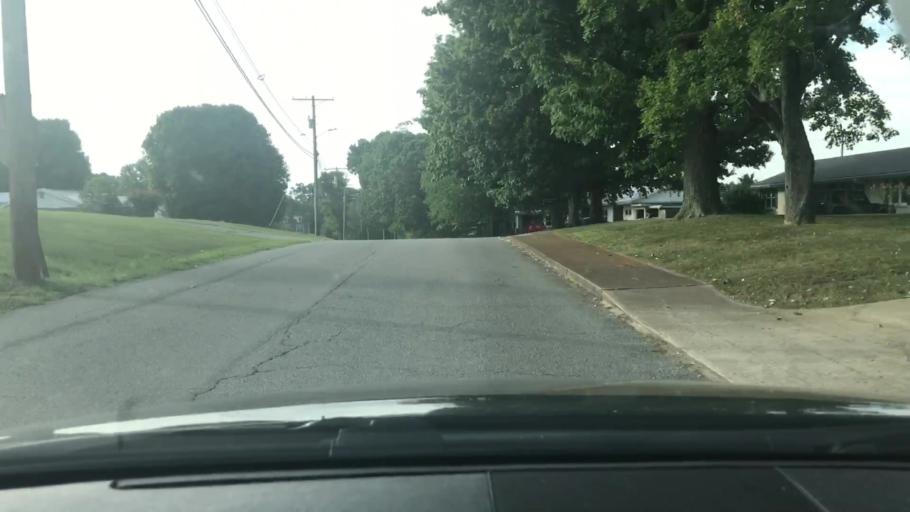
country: US
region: Tennessee
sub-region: Dickson County
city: White Bluff
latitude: 36.1098
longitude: -87.2236
